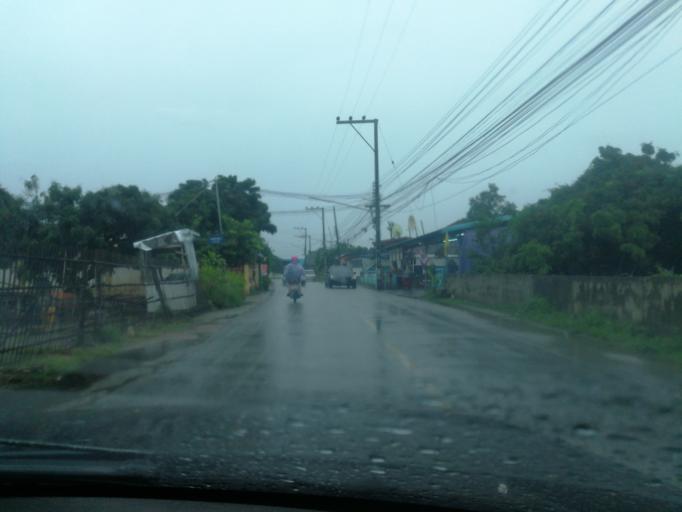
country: TH
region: Chiang Mai
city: San Pa Tong
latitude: 18.6127
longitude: 98.9045
